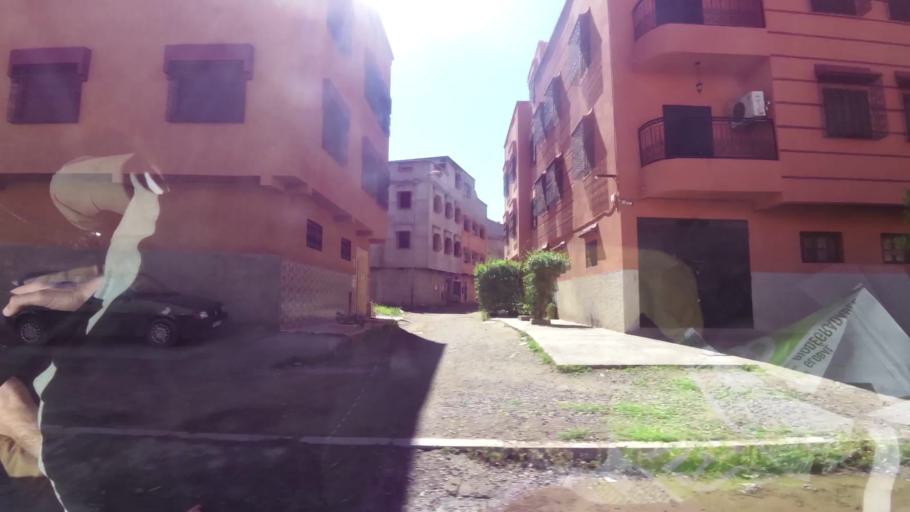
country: MA
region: Marrakech-Tensift-Al Haouz
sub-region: Marrakech
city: Marrakesh
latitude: 31.5782
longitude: -8.0568
